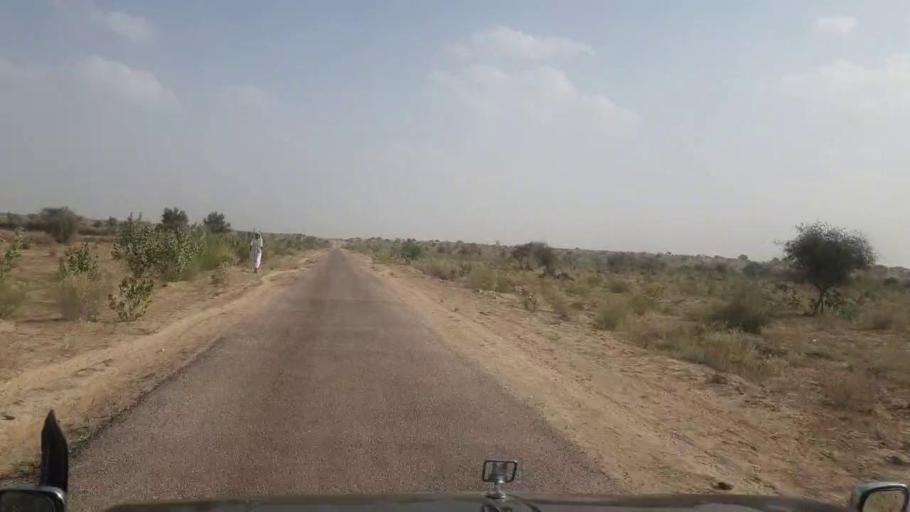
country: PK
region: Sindh
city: Islamkot
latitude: 25.1462
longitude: 70.3126
